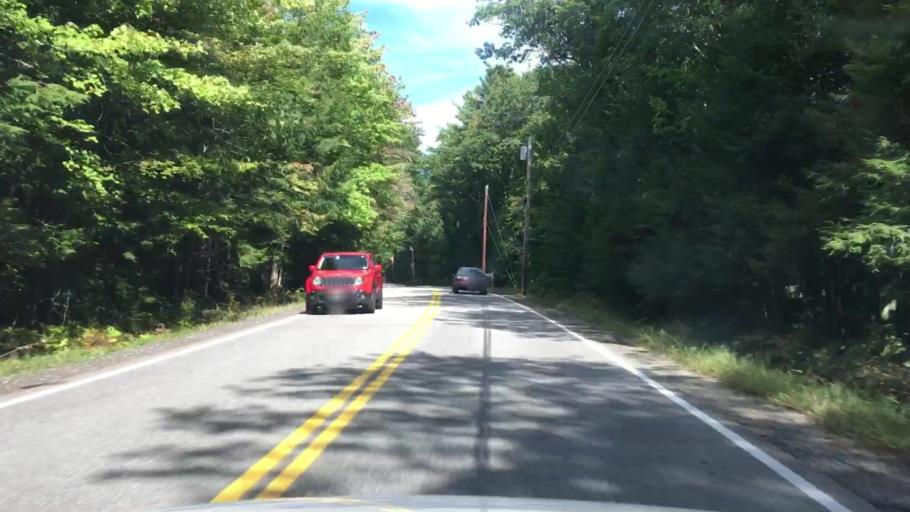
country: US
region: Maine
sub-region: Cumberland County
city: West Scarborough
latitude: 43.5885
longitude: -70.4368
